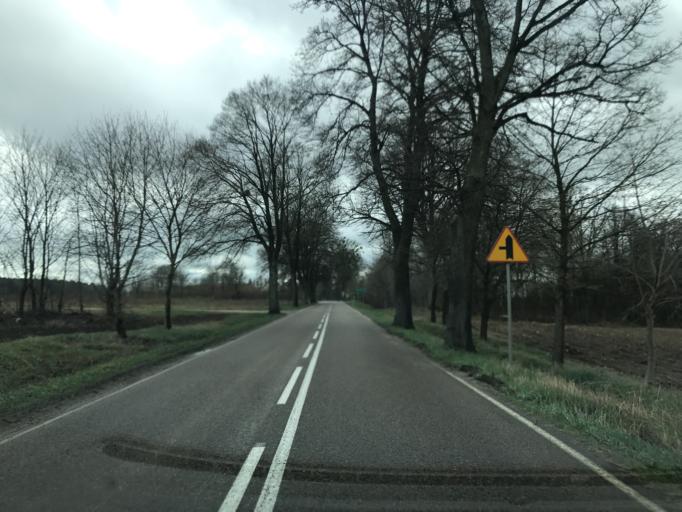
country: PL
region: Warmian-Masurian Voivodeship
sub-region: Powiat olsztynski
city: Olsztynek
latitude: 53.5303
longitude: 20.2502
